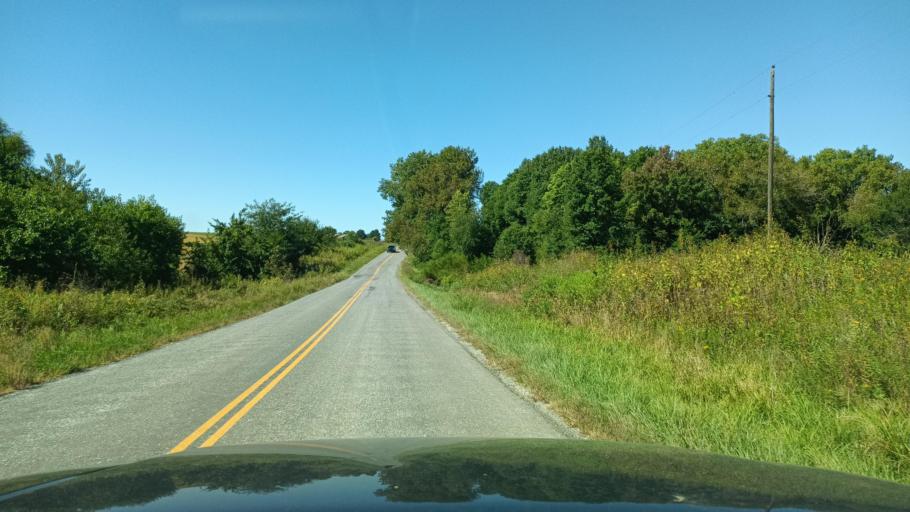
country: US
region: Missouri
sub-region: Adair County
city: Kirksville
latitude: 40.3306
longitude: -92.5044
